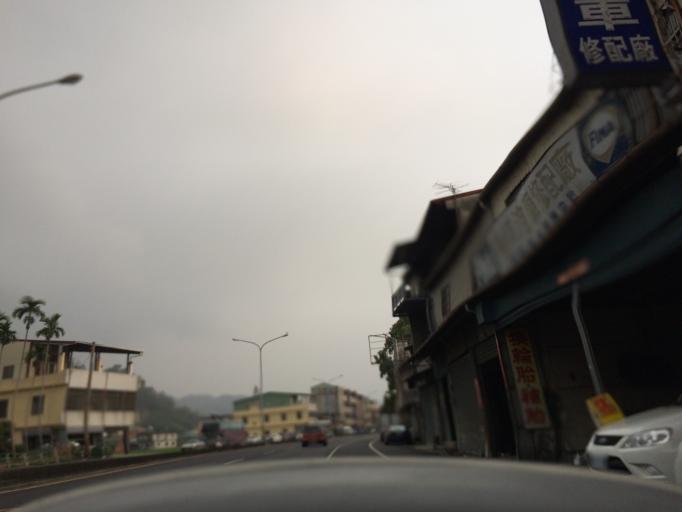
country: TW
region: Taiwan
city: Zhongxing New Village
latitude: 24.0402
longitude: 120.6925
